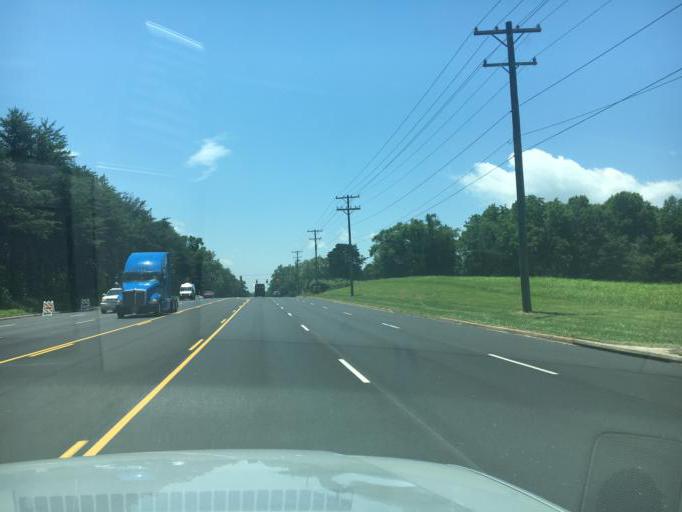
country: US
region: South Carolina
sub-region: Greenville County
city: Travelers Rest
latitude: 34.9384
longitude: -82.4454
